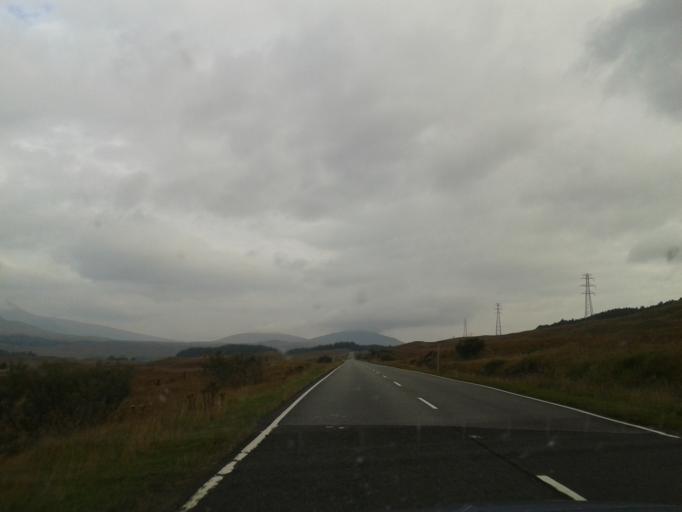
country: GB
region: Scotland
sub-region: Highland
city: Spean Bridge
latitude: 56.5256
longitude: -4.7670
